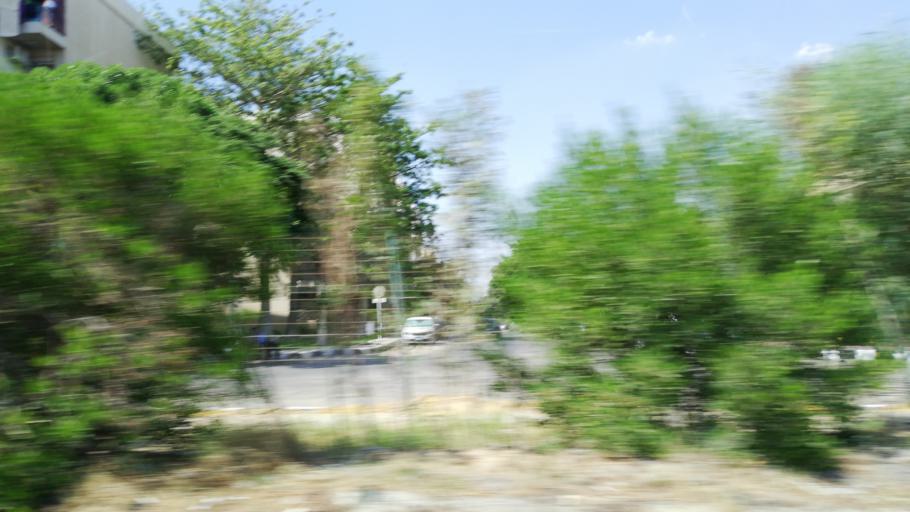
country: EG
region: Muhafazat al Qalyubiyah
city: Al Khankah
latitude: 30.0535
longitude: 31.4962
